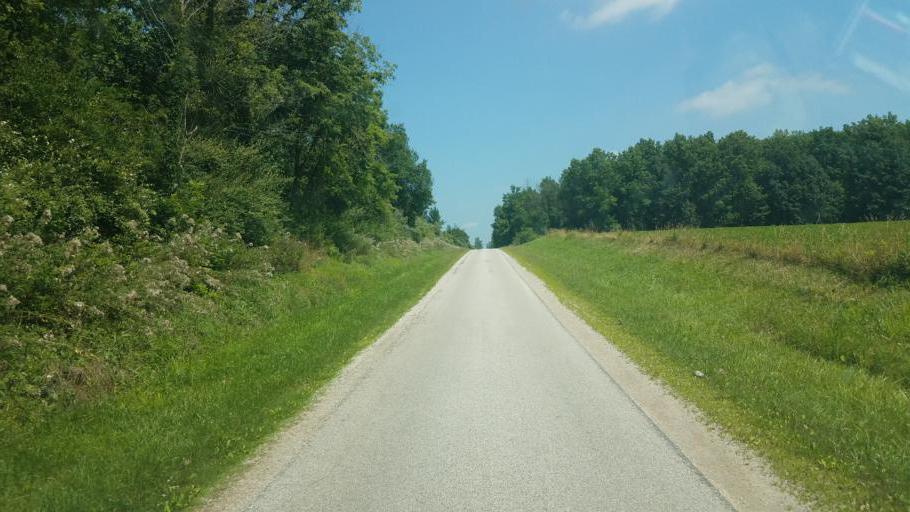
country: US
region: Ohio
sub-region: Seneca County
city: Tiffin
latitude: 41.0550
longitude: -82.9771
